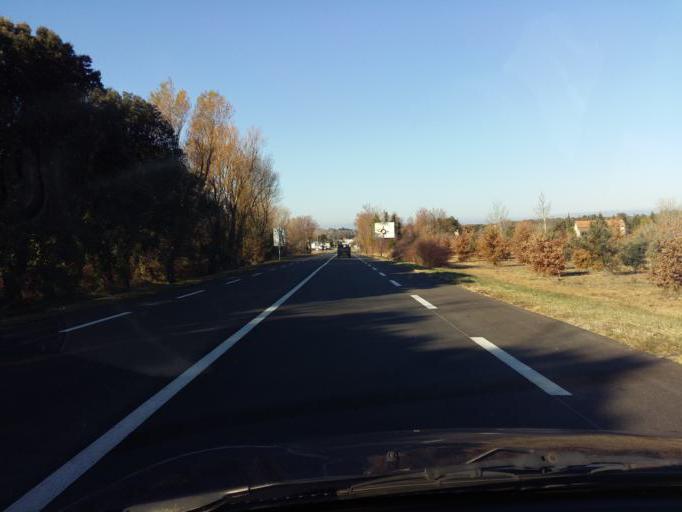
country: FR
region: Provence-Alpes-Cote d'Azur
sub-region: Departement du Vaucluse
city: Grillon
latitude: 44.3932
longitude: 4.9456
